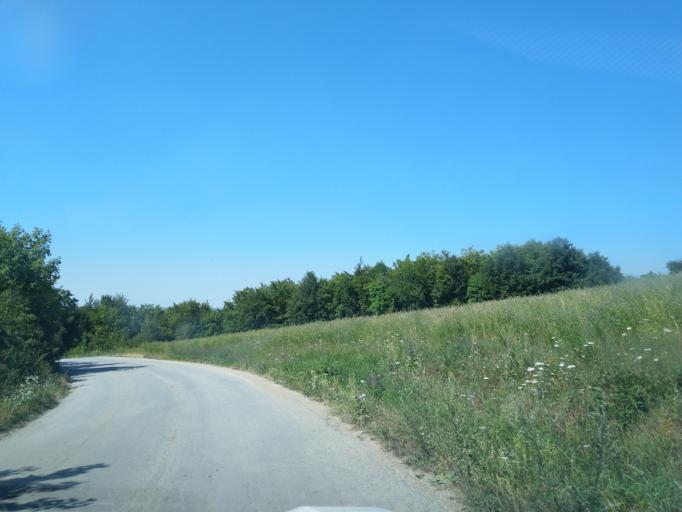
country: RS
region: Central Serbia
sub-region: Zlatiborski Okrug
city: Uzice
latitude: 43.8169
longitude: 19.8566
